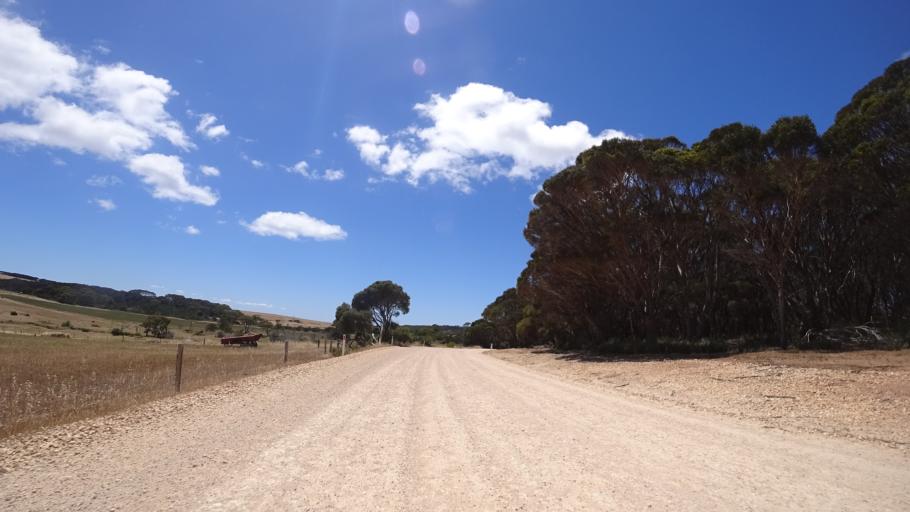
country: AU
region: South Australia
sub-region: Kangaroo Island
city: Kingscote
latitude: -35.8224
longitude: 138.0356
